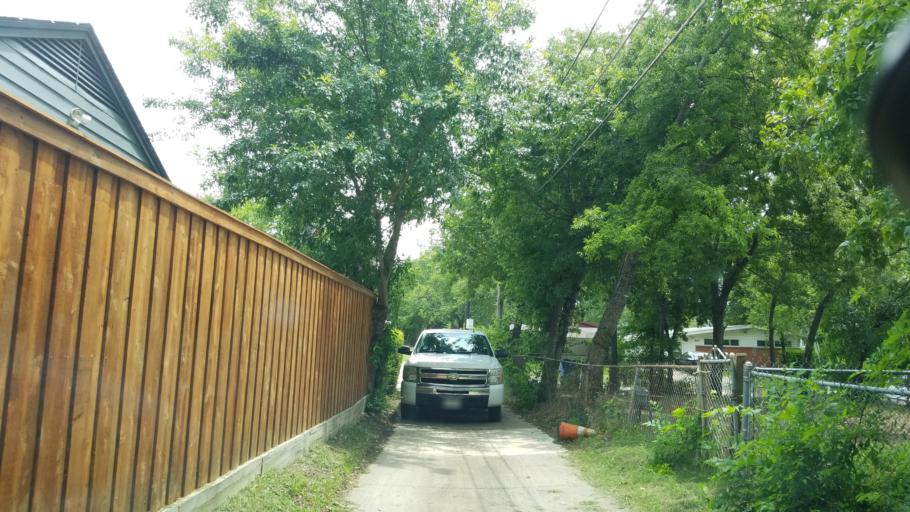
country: US
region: Texas
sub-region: Dallas County
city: Farmers Branch
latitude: 32.8754
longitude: -96.8641
